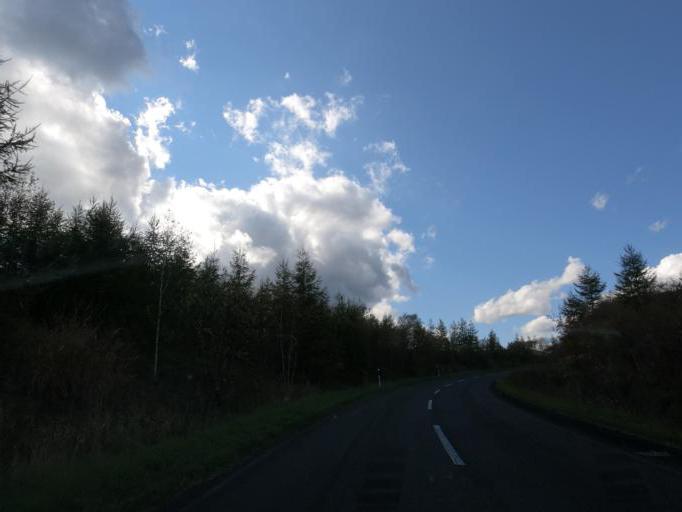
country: JP
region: Hokkaido
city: Otofuke
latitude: 43.2766
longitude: 143.2365
